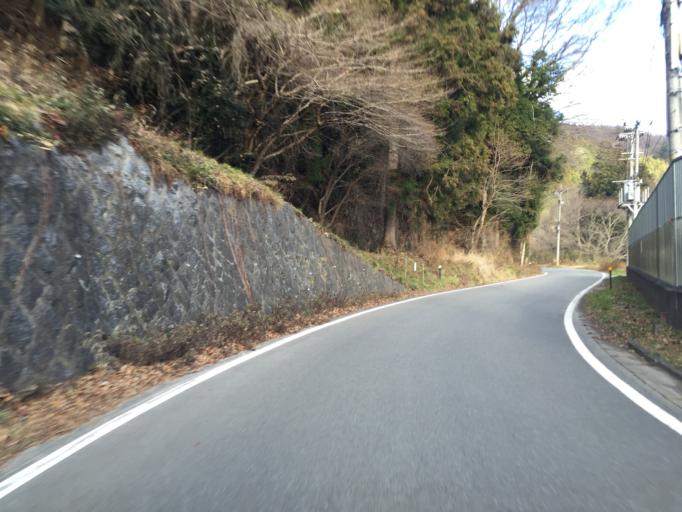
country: JP
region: Fukushima
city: Funehikimachi-funehiki
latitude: 37.2339
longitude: 140.6929
